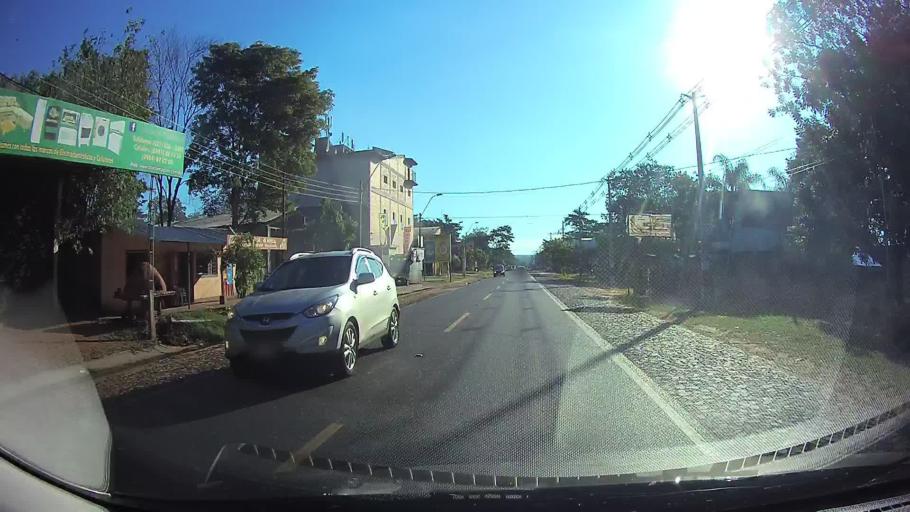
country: PY
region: Central
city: Aregua
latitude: -25.2963
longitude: -57.4266
